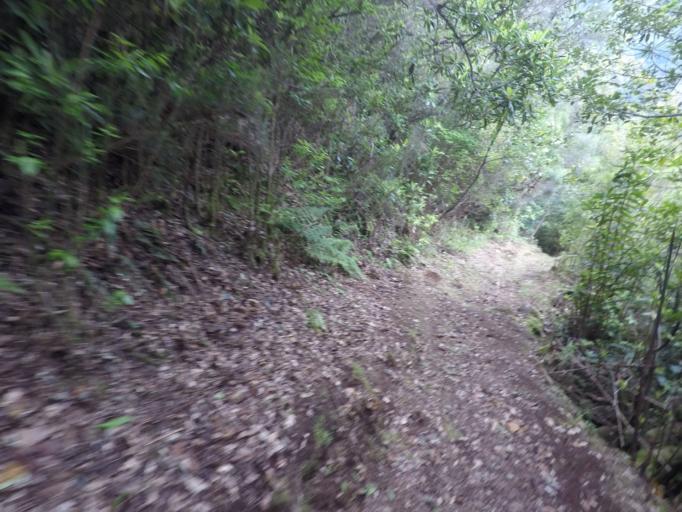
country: PT
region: Madeira
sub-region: Camara de Lobos
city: Curral das Freiras
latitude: 32.7760
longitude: -16.9809
